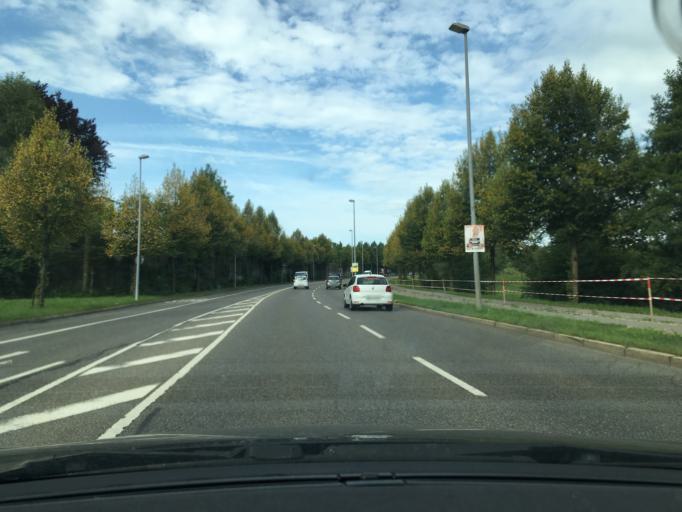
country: DE
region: Baden-Wuerttemberg
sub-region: Tuebingen Region
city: Ravensburg
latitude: 47.7817
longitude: 9.5970
